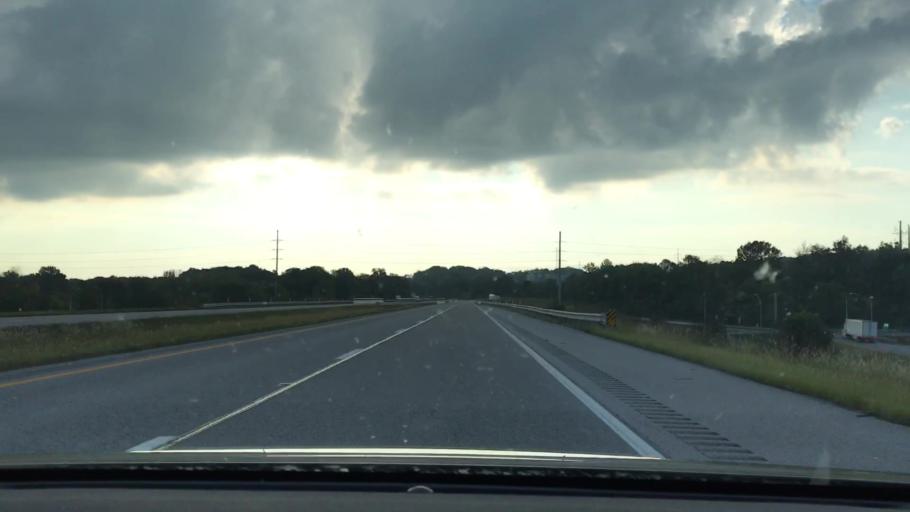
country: US
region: Kentucky
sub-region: Barren County
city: Glasgow
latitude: 36.9791
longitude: -85.9369
